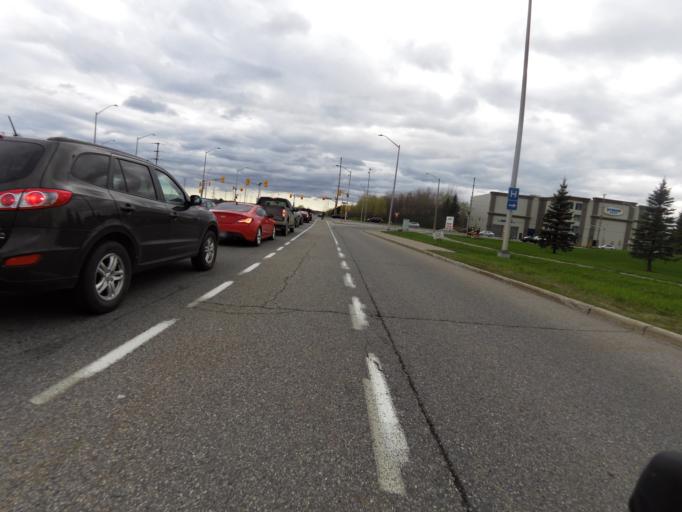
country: CA
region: Ontario
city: Bells Corners
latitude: 45.3226
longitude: -75.7761
